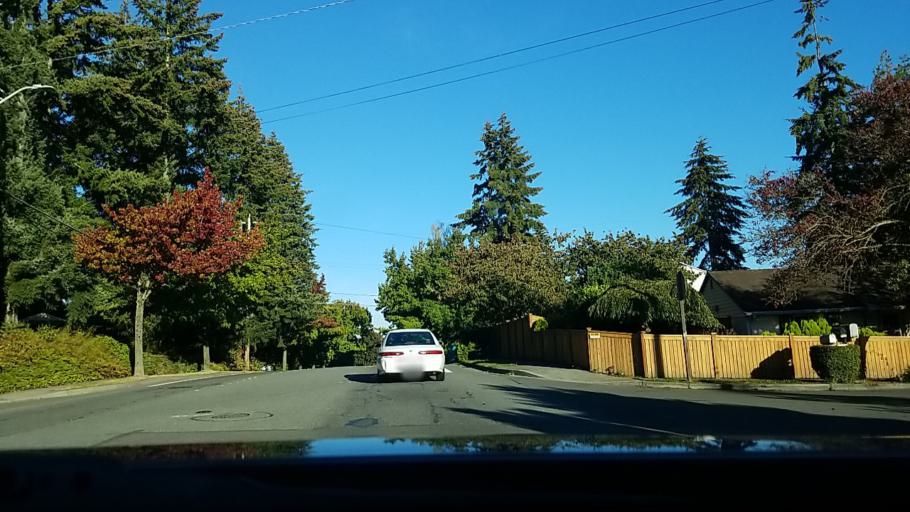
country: US
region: Washington
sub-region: King County
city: Shoreline
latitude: 47.7414
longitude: -122.3428
